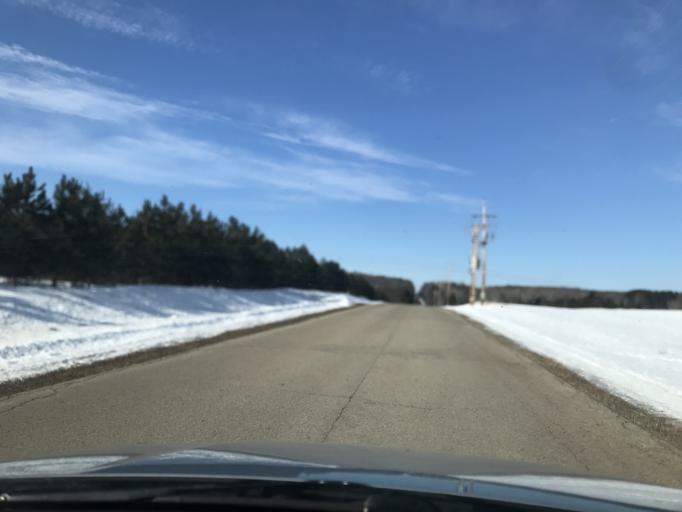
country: US
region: Wisconsin
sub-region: Oconto County
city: Gillett
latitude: 44.9615
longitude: -88.2699
